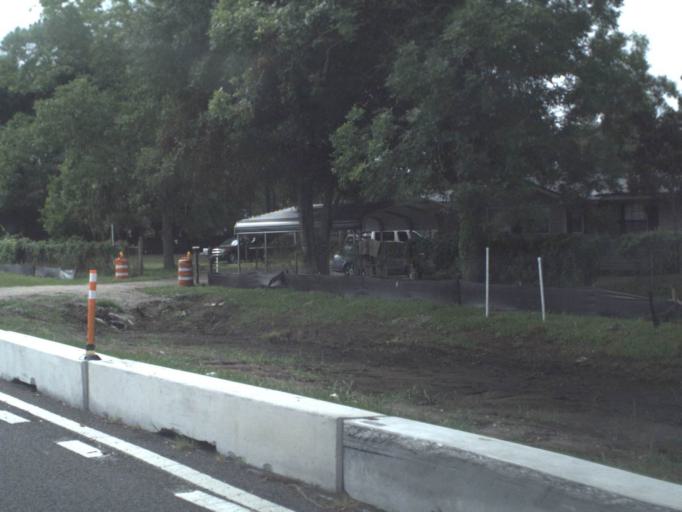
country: US
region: Florida
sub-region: Nassau County
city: Fernandina Beach
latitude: 30.6179
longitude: -81.5168
